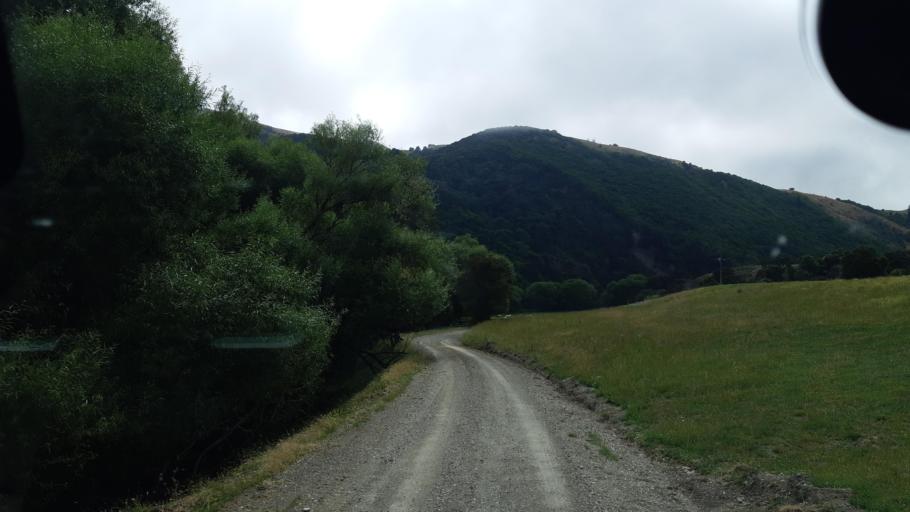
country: NZ
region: Marlborough
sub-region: Marlborough District
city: Blenheim
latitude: -41.9708
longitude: 173.9904
